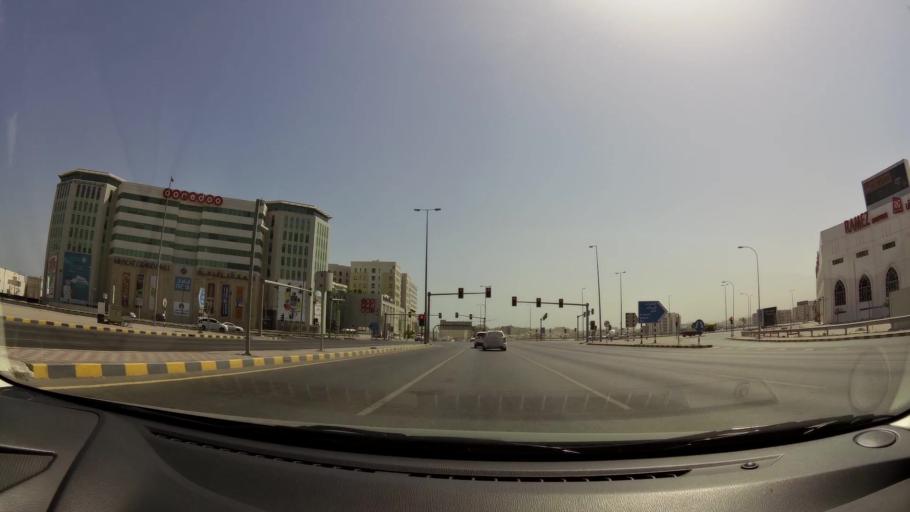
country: OM
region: Muhafazat Masqat
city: Bawshar
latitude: 23.5871
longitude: 58.4125
